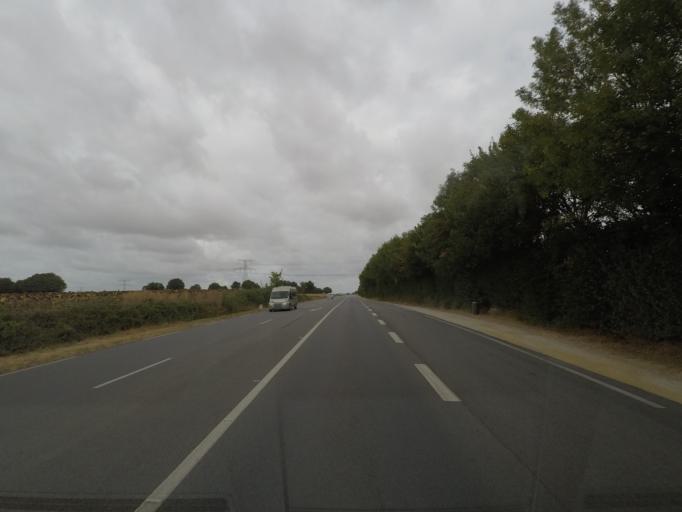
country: FR
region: Poitou-Charentes
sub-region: Departement des Deux-Sevres
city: Thorigne
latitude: 46.2745
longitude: -0.2399
